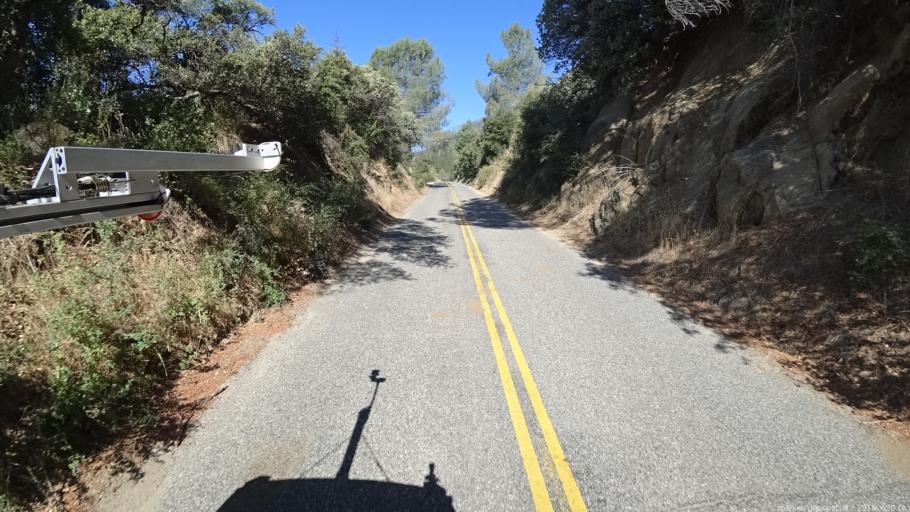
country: US
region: California
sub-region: Fresno County
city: Auberry
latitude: 37.2171
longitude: -119.3697
